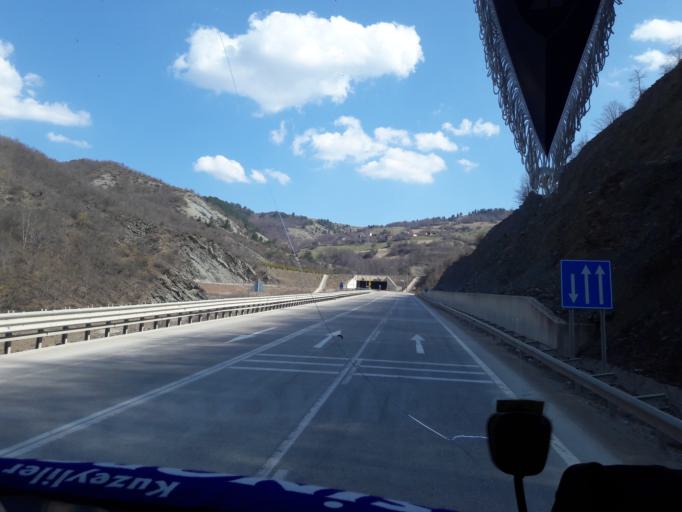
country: TR
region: Sinop
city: Erfelek
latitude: 41.6767
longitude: 34.9124
